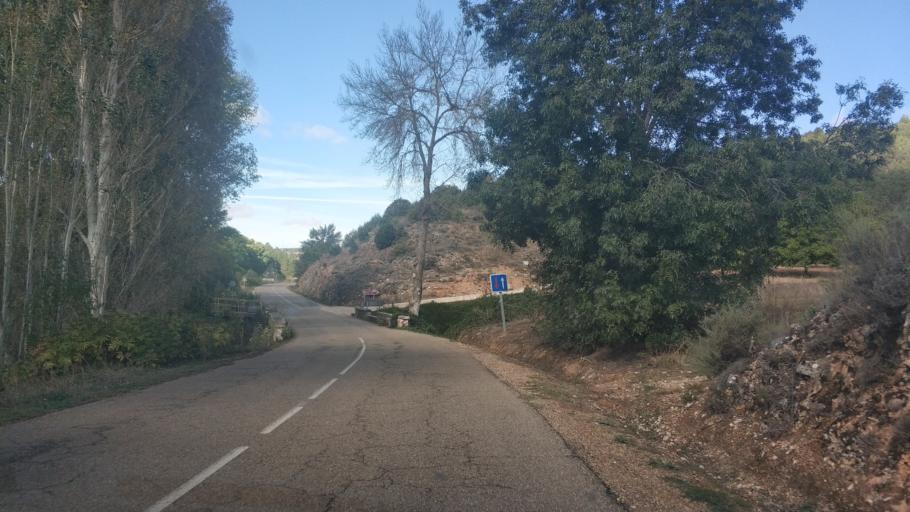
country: ES
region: Castille and Leon
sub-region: Provincia de Burgos
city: Covarrubias
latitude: 42.0536
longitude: -3.5060
